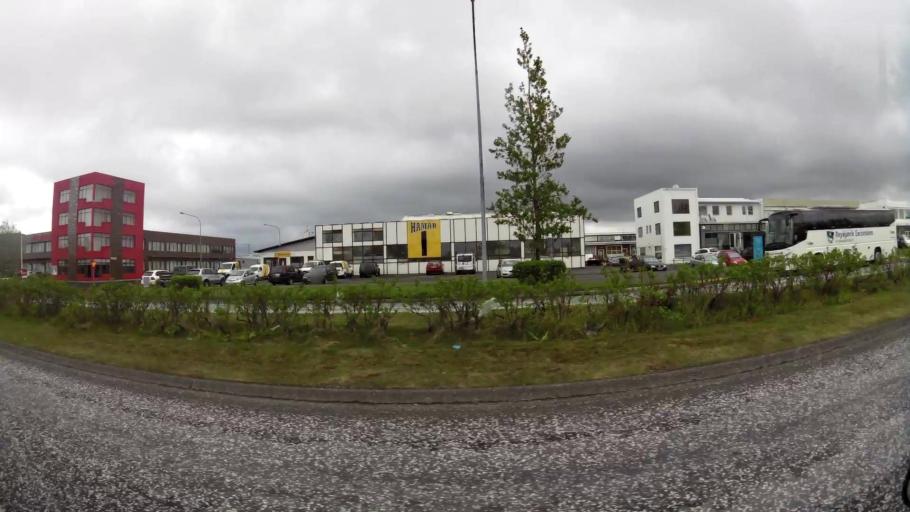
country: IS
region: Capital Region
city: Hafnarfjoerdur
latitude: 64.0799
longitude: -21.9492
